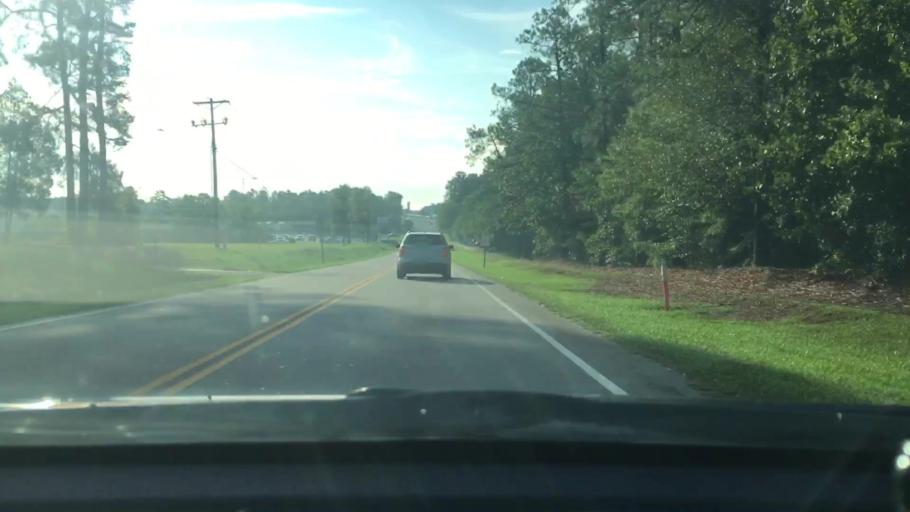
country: US
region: South Carolina
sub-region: Lexington County
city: Irmo
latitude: 34.1043
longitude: -81.1852
